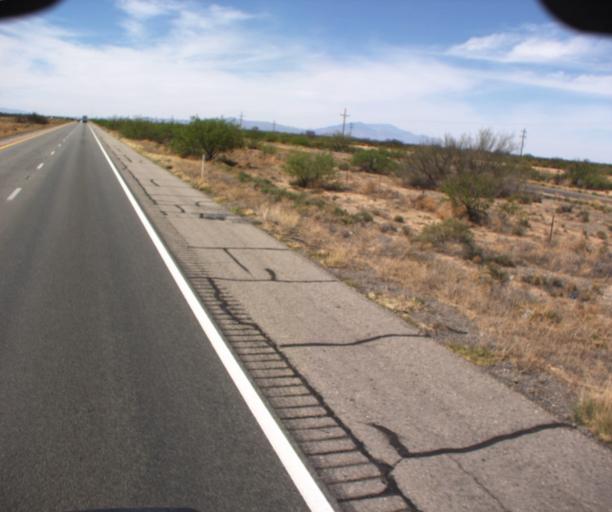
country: US
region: Arizona
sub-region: Cochise County
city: Willcox
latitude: 32.2992
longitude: -109.3615
